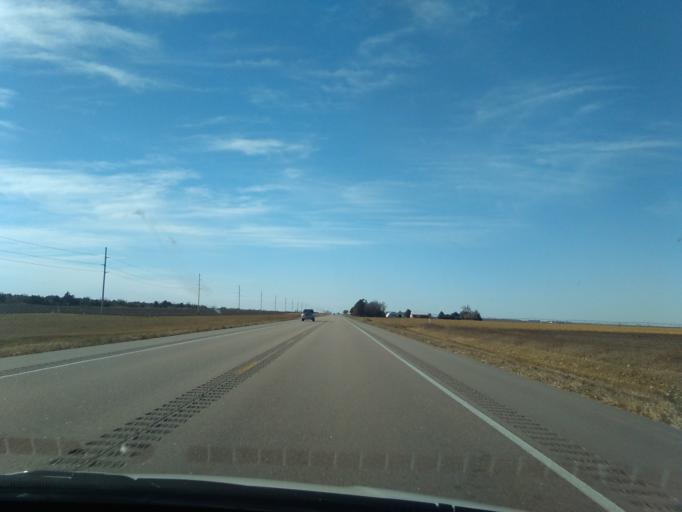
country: US
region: Nebraska
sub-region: Clay County
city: Harvard
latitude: 40.5828
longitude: -98.1550
